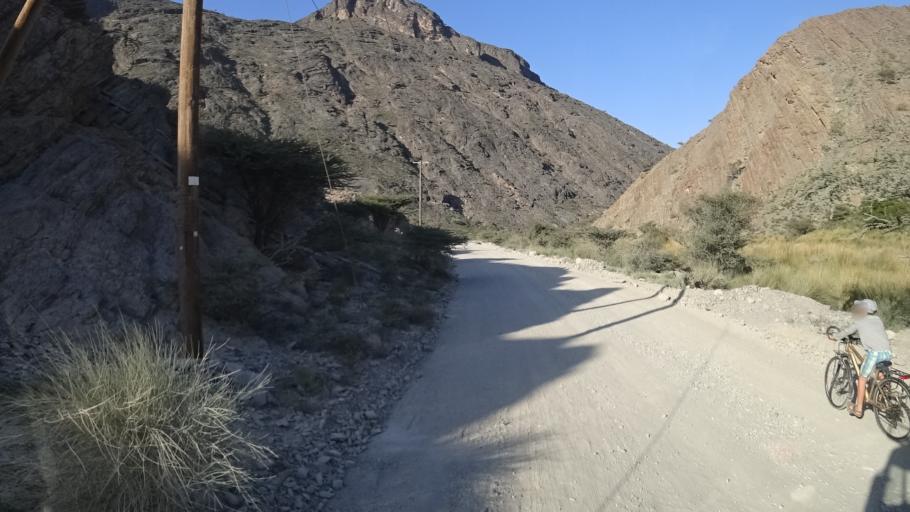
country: OM
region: Al Batinah
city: Bayt al `Awabi
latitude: 23.2321
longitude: 57.4258
